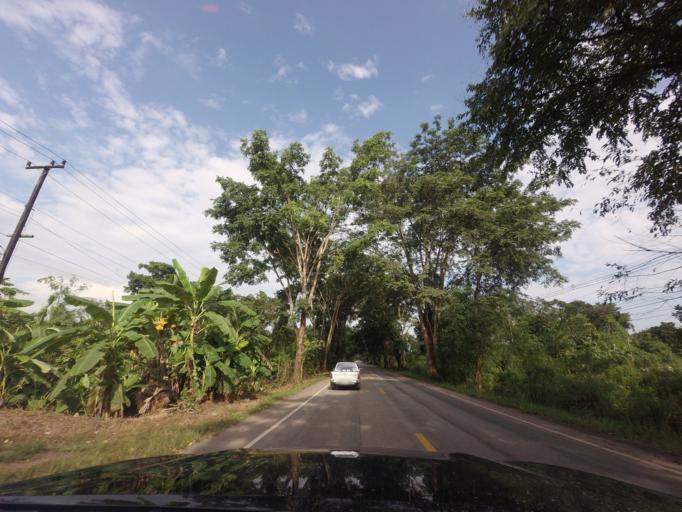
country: TH
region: Nong Khai
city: Pho Tak
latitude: 17.7866
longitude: 102.3680
